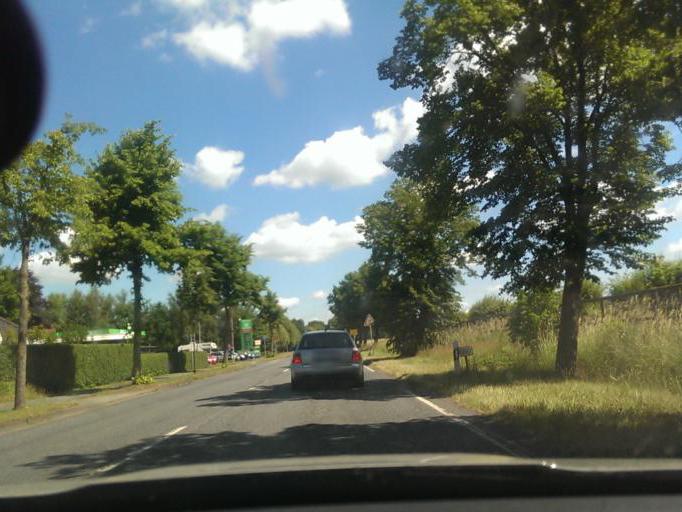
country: DE
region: Lower Saxony
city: Verden
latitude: 52.9780
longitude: 9.2578
